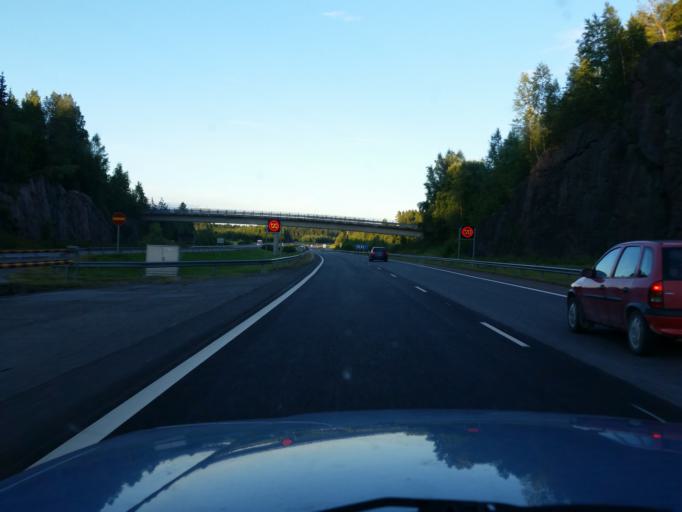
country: FI
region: Varsinais-Suomi
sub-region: Turku
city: Piikkioe
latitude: 60.4449
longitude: 22.5479
